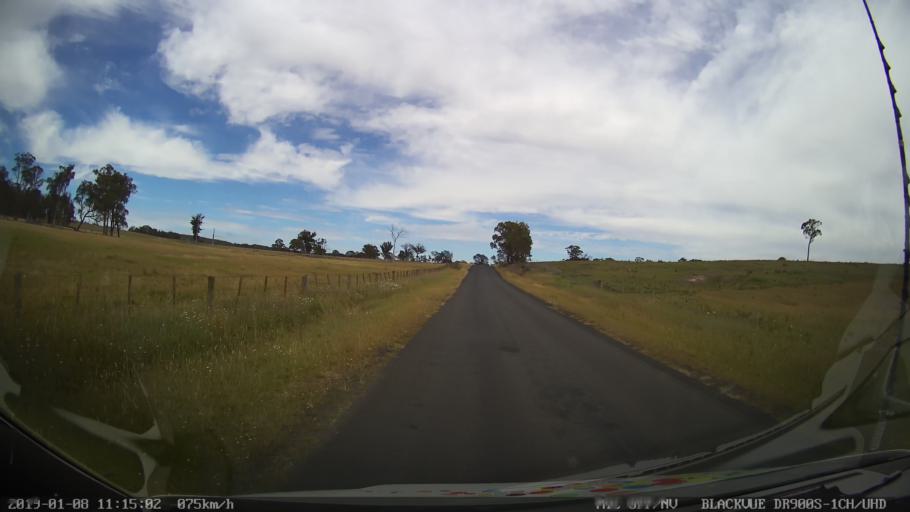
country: AU
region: New South Wales
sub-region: Guyra
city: Guyra
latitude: -30.2242
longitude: 151.5820
